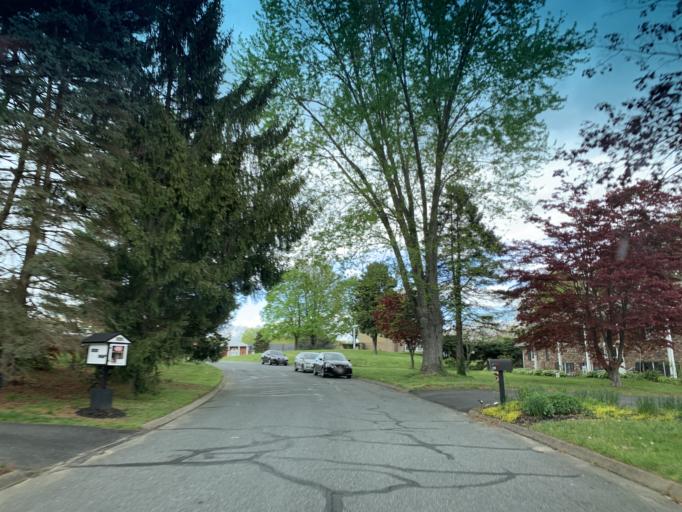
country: US
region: Maryland
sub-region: Harford County
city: Pleasant Hills
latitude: 39.4950
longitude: -76.3618
